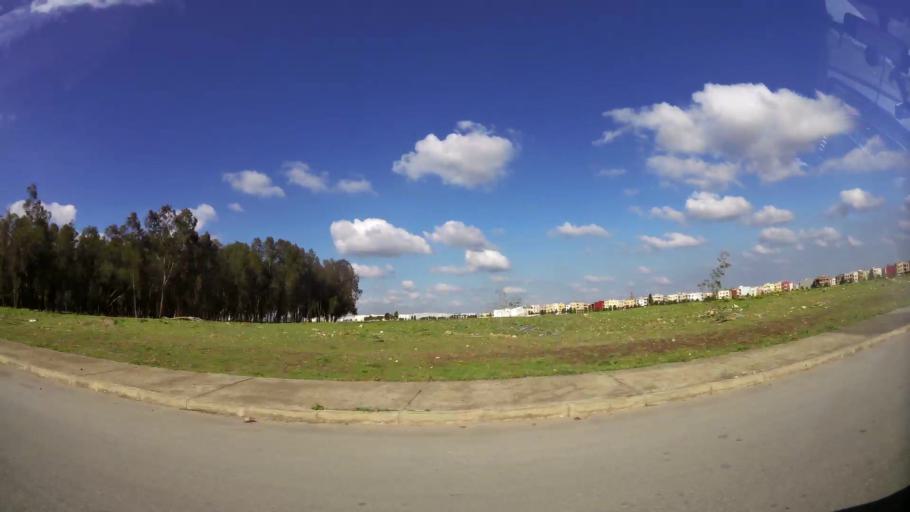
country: MA
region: Chaouia-Ouardigha
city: Nouaseur
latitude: 33.3872
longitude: -7.5523
